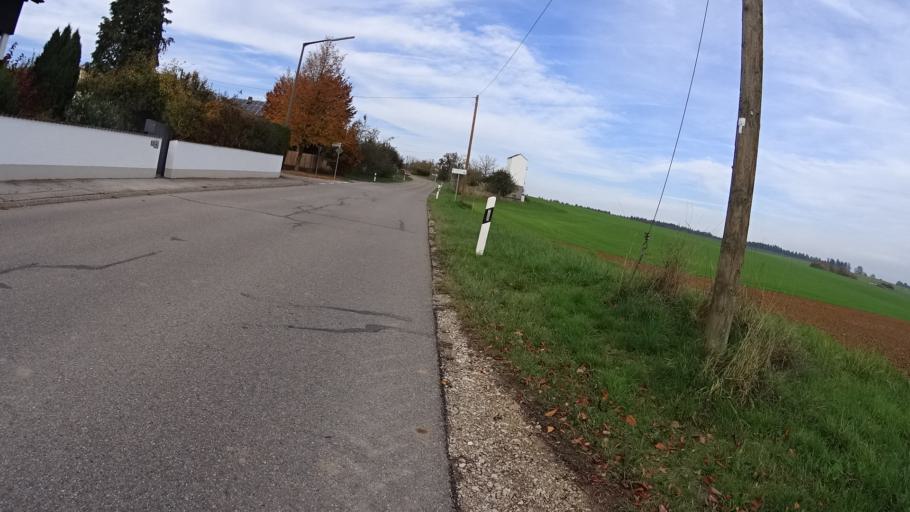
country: DE
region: Bavaria
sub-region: Upper Bavaria
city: Buxheim
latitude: 48.8289
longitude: 11.2754
